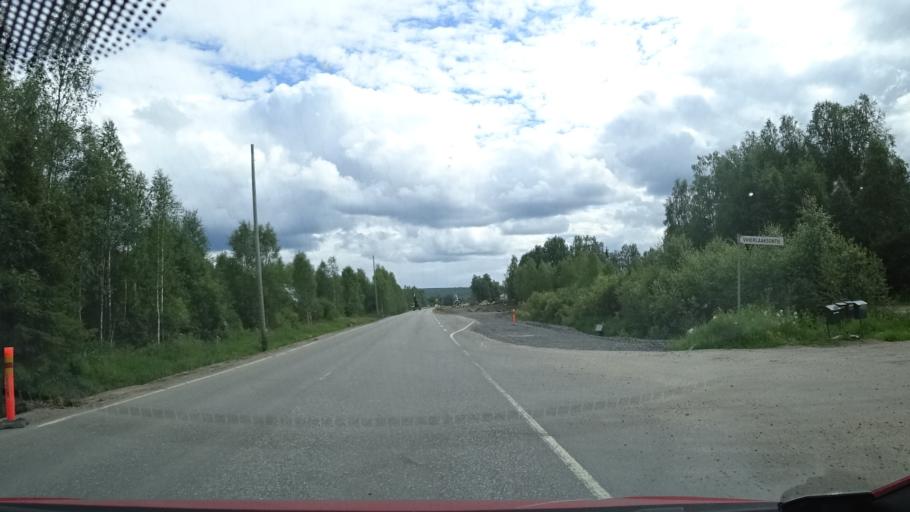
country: FI
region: Lapland
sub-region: Rovaniemi
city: Rovaniemi
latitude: 66.5296
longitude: 25.7386
